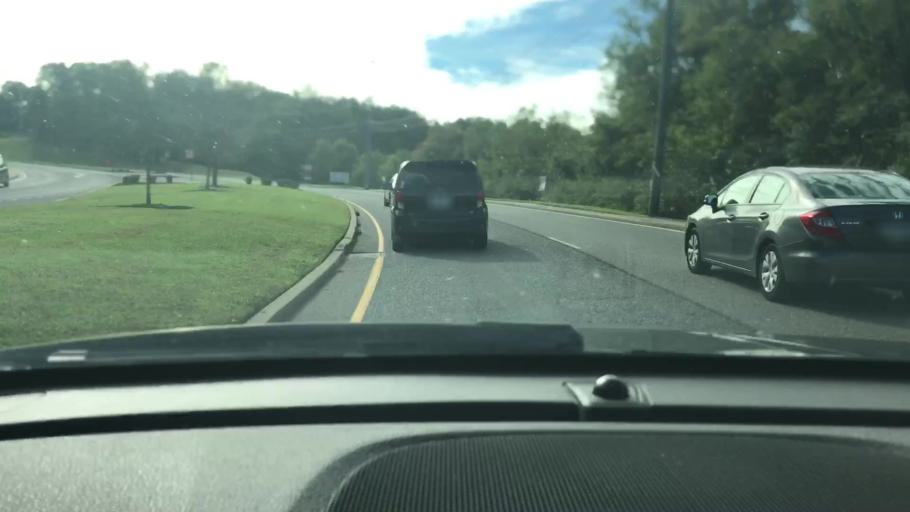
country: US
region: Tennessee
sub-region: Davidson County
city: Goodlettsville
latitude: 36.3128
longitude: -86.6989
